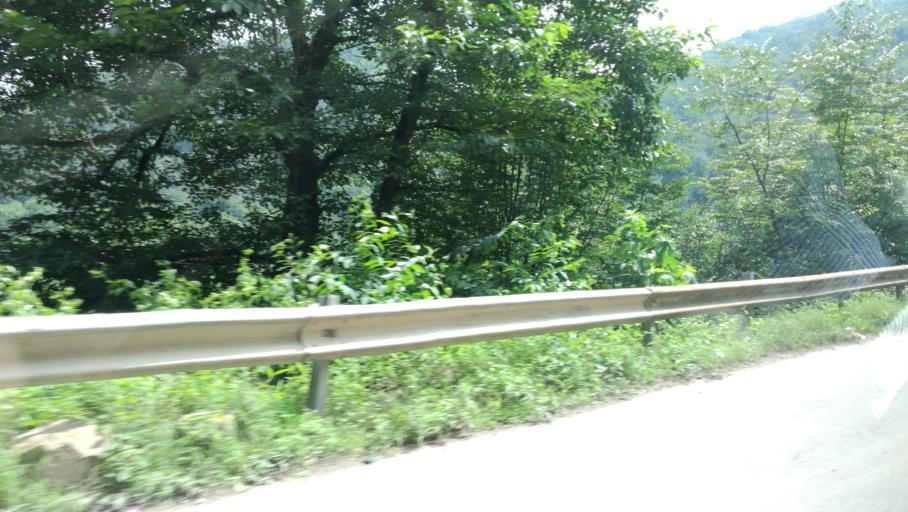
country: IR
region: Mazandaran
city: Ramsar
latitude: 36.8934
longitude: 50.5799
